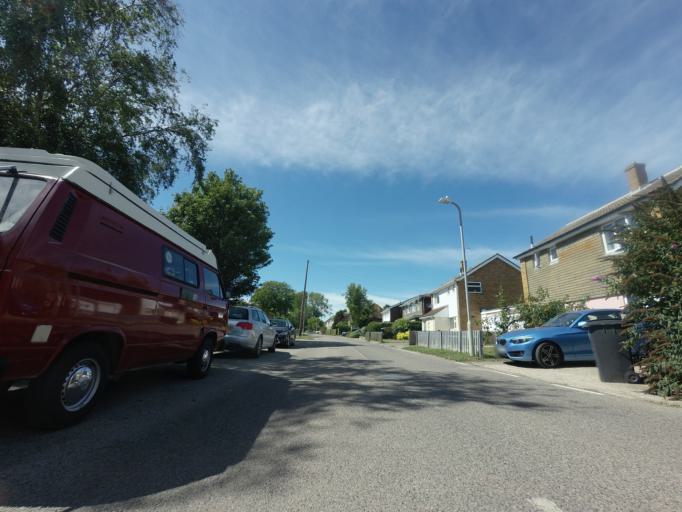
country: GB
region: England
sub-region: Kent
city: Sandwich
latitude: 51.2702
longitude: 1.3621
